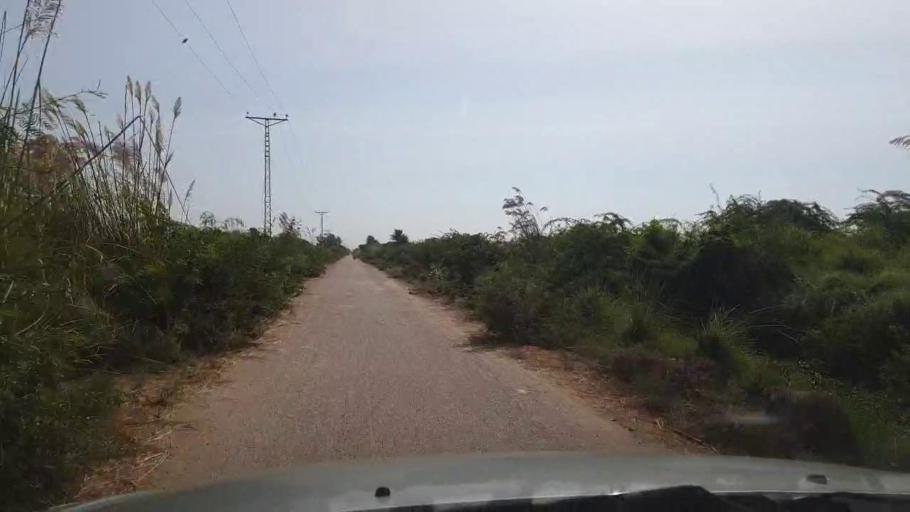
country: PK
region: Sindh
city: Tando Muhammad Khan
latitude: 25.1554
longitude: 68.3810
